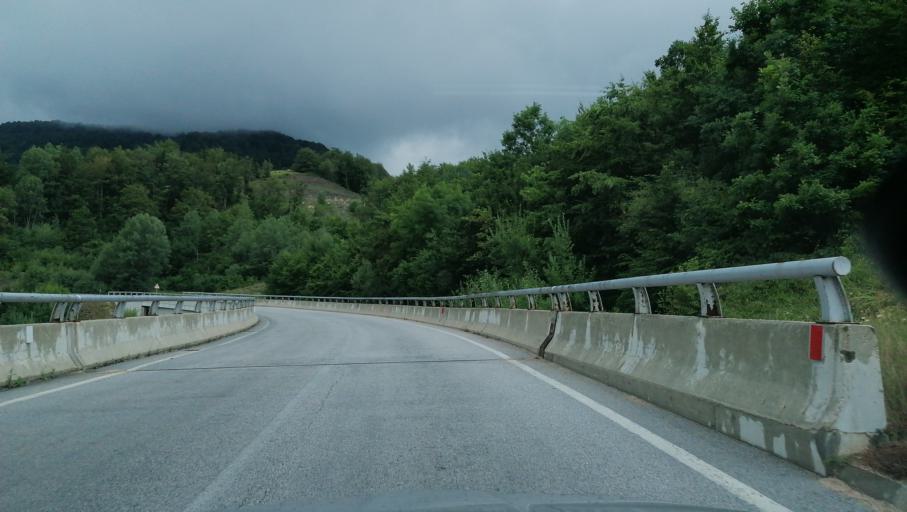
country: BA
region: Republika Srpska
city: Gacko
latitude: 43.2540
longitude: 18.6265
